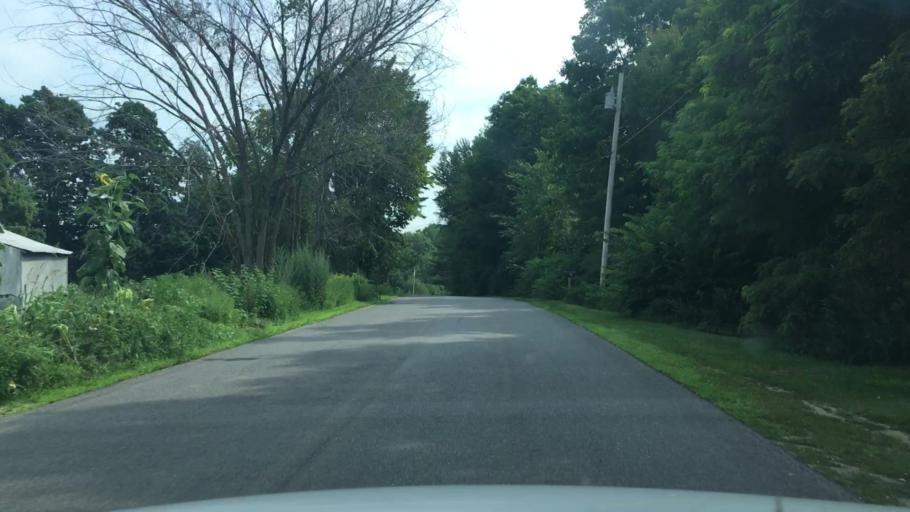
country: US
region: Maine
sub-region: Lincoln County
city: Jefferson
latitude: 44.2354
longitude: -69.4440
